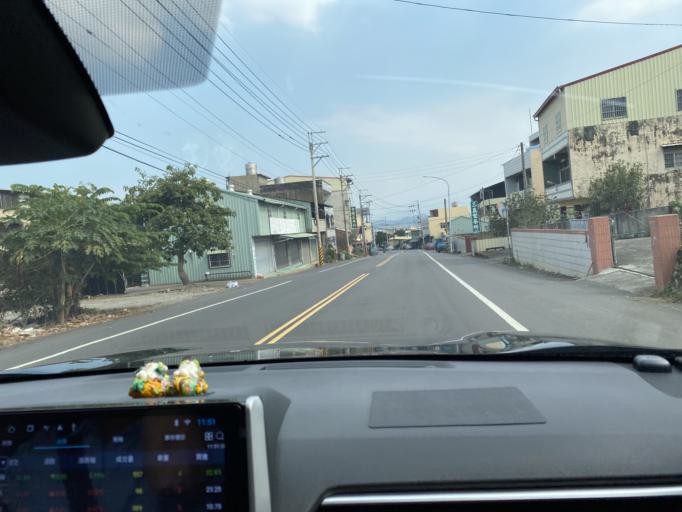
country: TW
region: Taiwan
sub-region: Nantou
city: Nantou
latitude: 23.8350
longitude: 120.6590
